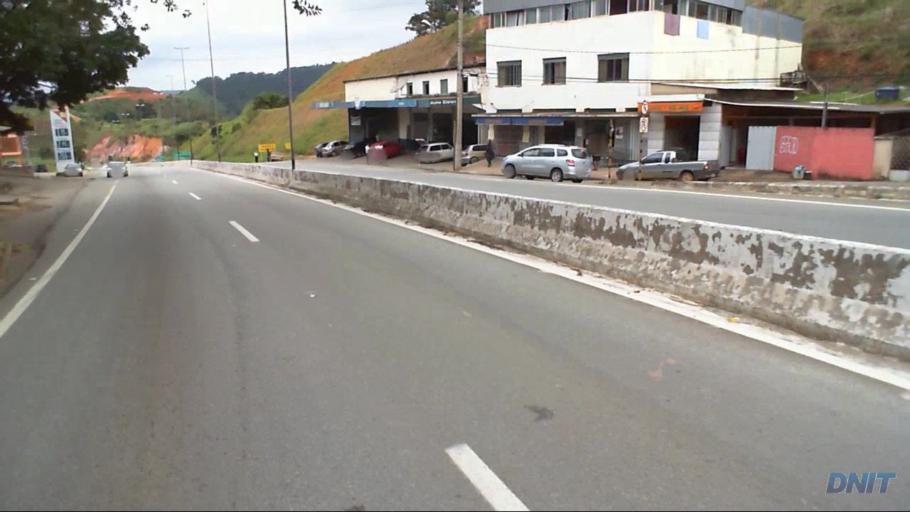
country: BR
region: Minas Gerais
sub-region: Nova Era
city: Nova Era
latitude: -19.7595
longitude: -43.0292
